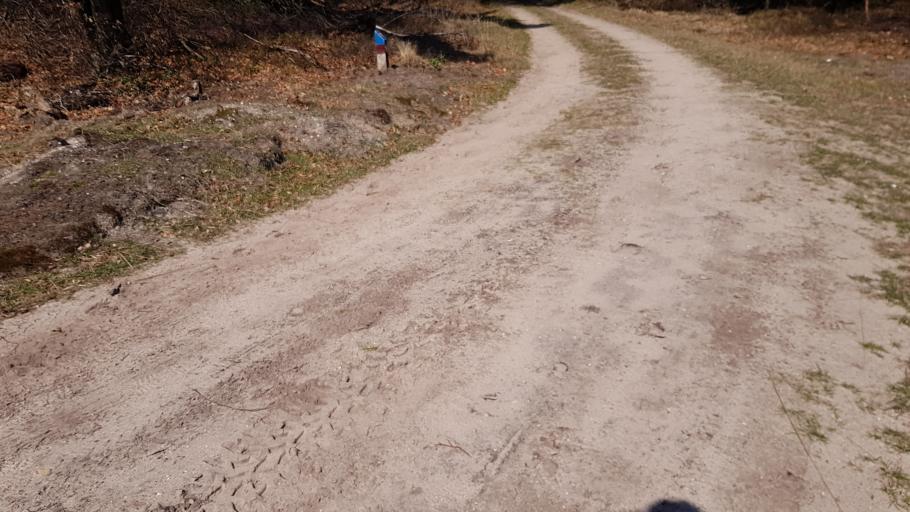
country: NL
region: Gelderland
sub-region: Gemeente Rheden
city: Rheden
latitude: 52.0543
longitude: 5.9996
